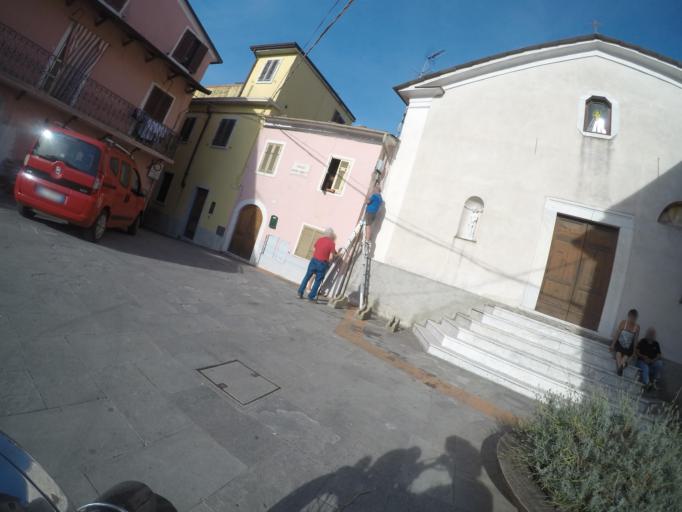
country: IT
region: Tuscany
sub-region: Provincia di Massa-Carrara
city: Carrara
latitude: 44.0887
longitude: 10.0907
